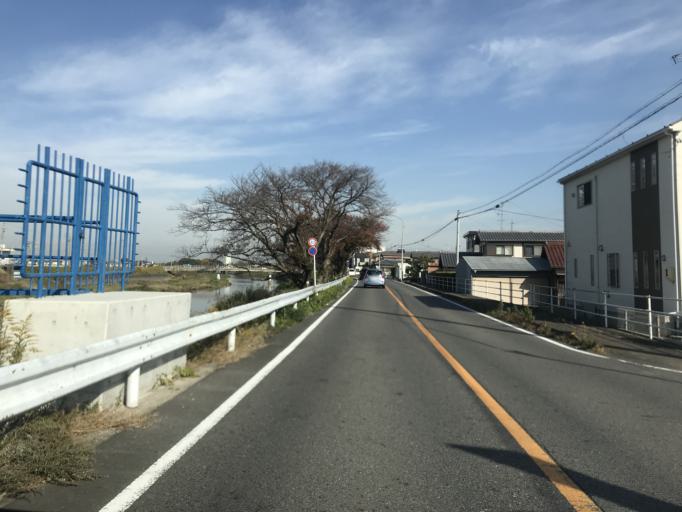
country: JP
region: Aichi
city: Iwakura
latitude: 35.2241
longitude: 136.8460
